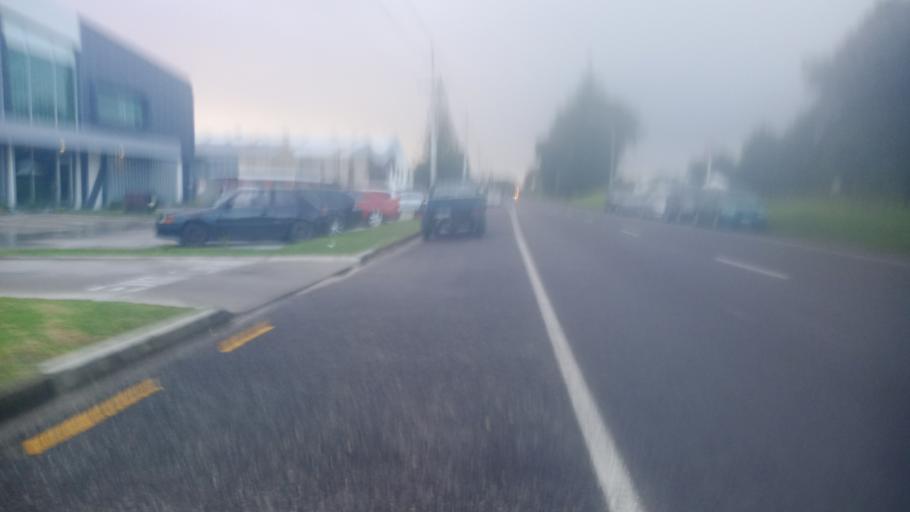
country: NZ
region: Gisborne
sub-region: Gisborne District
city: Gisborne
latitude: -38.6669
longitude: 177.9941
